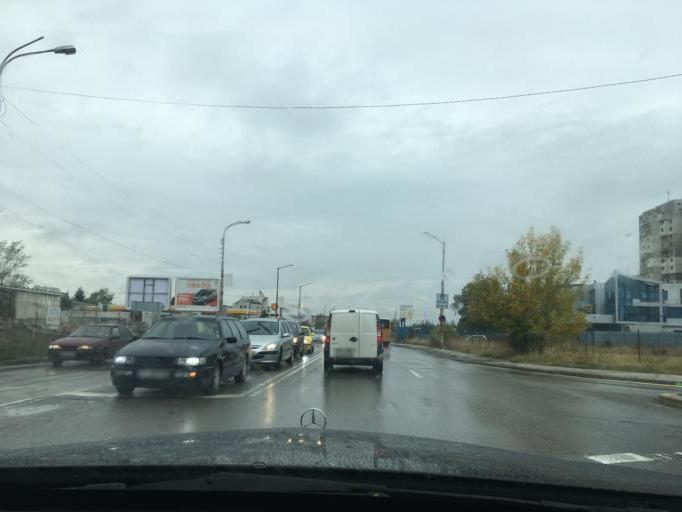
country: BG
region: Sofiya
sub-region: Obshtina Bozhurishte
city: Bozhurishte
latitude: 42.7334
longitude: 23.2503
